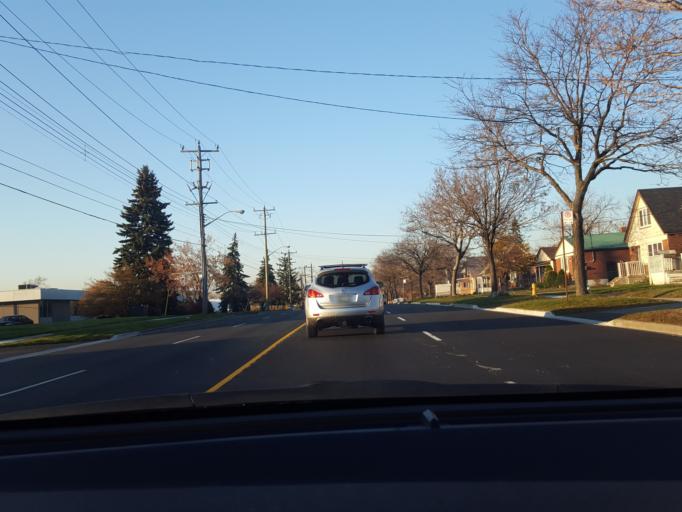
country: CA
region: Ontario
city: Scarborough
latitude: 43.7530
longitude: -79.2870
